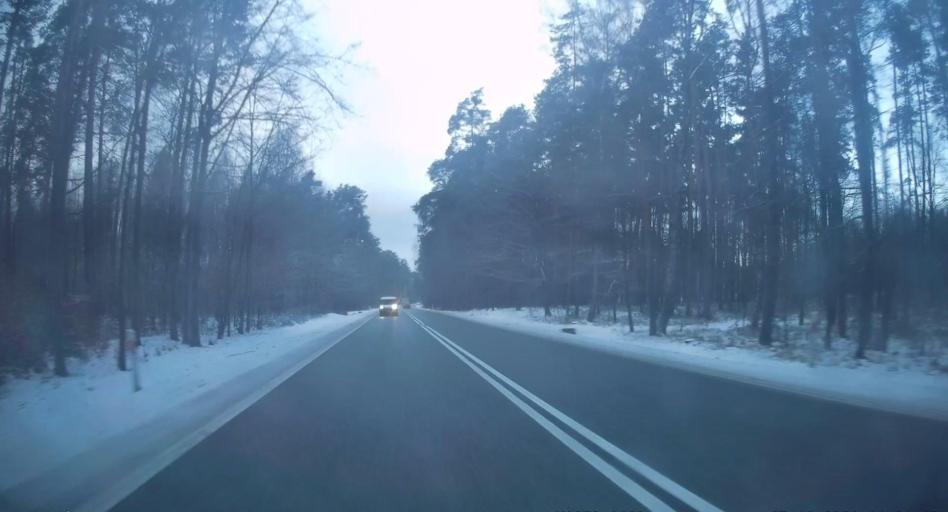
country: PL
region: Swietokrzyskie
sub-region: Powiat konecki
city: Radoszyce
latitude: 51.0983
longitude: 20.3292
